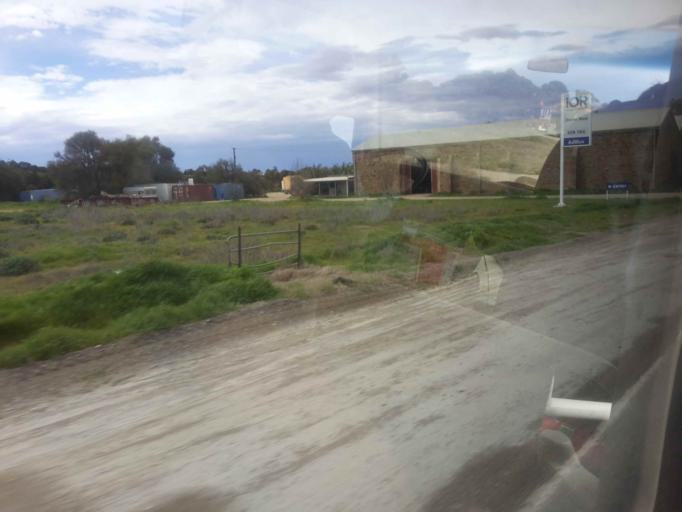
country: AU
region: South Australia
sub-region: Clare and Gilbert Valleys
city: Clare
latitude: -33.6695
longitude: 138.9211
